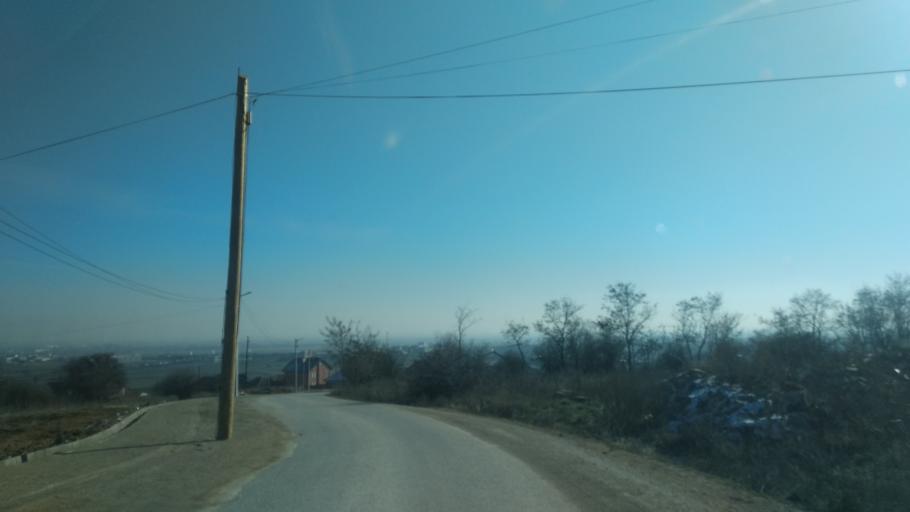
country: XK
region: Pristina
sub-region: Komuna e Gracanices
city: Glanica
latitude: 42.6076
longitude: 21.0254
